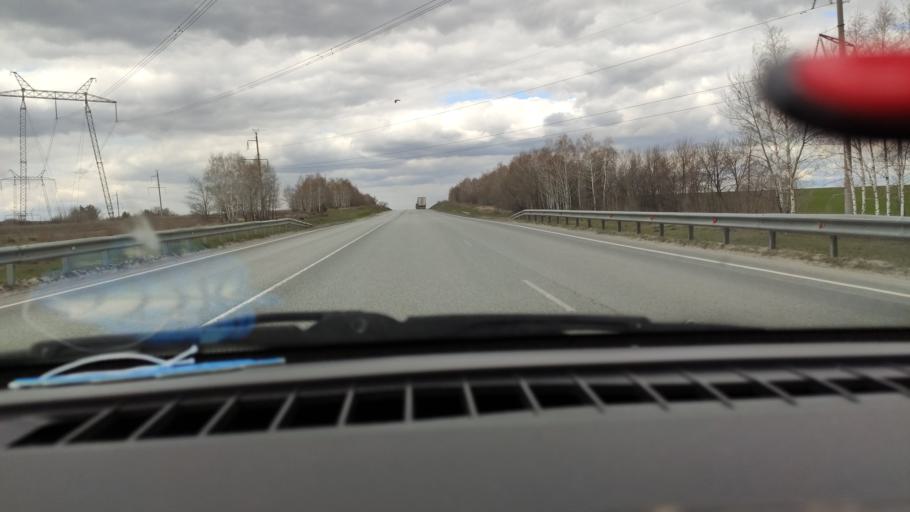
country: RU
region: Saratov
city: Tersa
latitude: 52.1026
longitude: 47.5007
